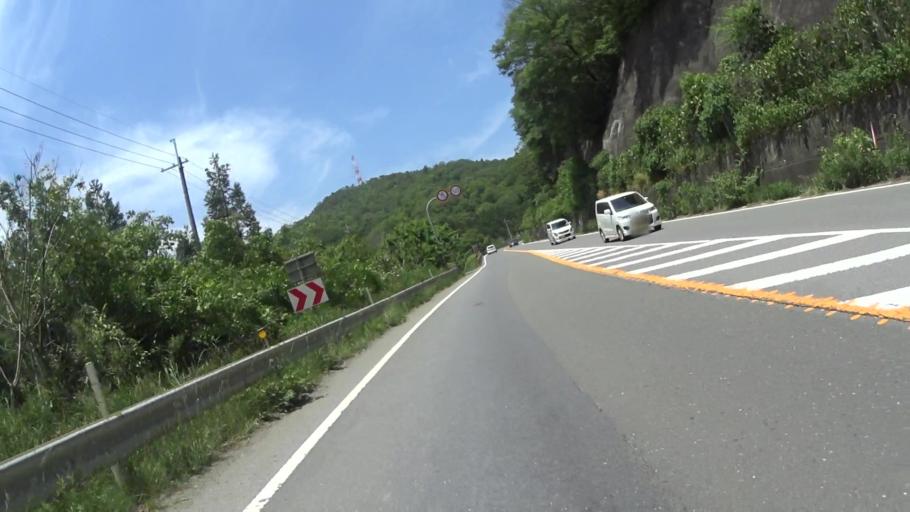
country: JP
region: Kyoto
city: Kameoka
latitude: 35.1196
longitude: 135.4521
